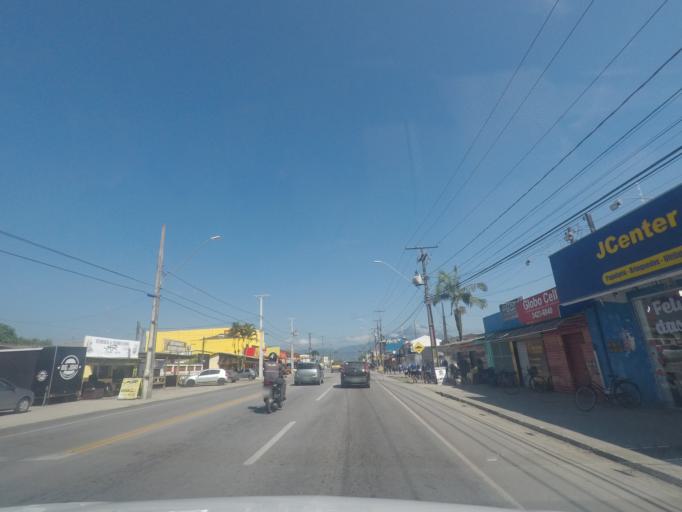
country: BR
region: Parana
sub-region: Paranagua
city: Paranagua
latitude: -25.5586
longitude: -48.5590
